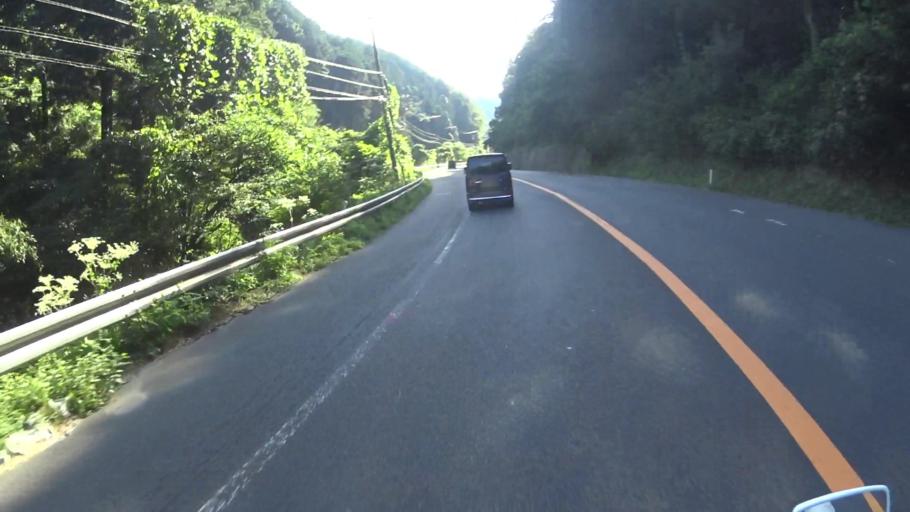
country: JP
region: Kyoto
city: Miyazu
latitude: 35.6626
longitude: 135.0111
